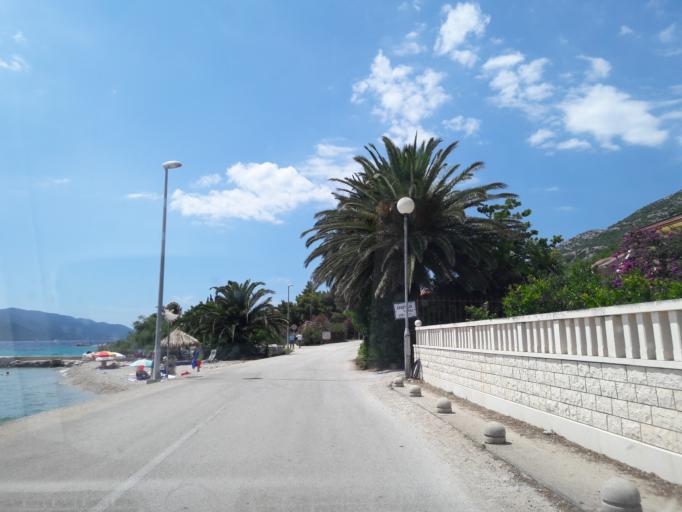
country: HR
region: Dubrovacko-Neretvanska
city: Korcula
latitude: 42.9746
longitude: 17.1390
